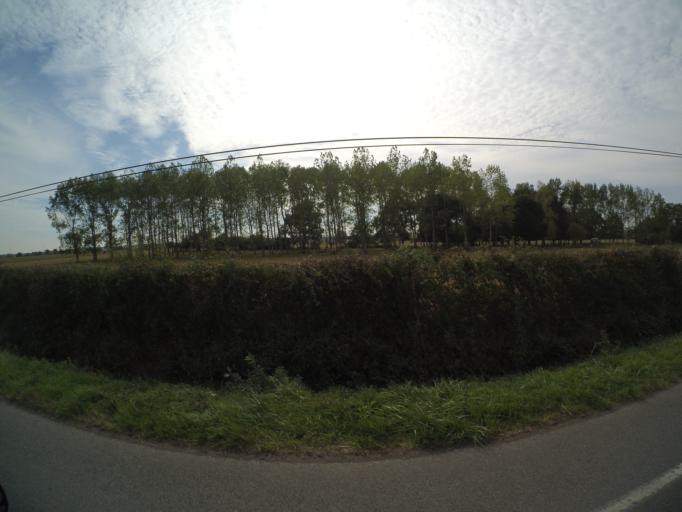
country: FR
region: Pays de la Loire
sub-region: Departement de Maine-et-Loire
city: Jallais
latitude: 47.1999
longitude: -0.8492
